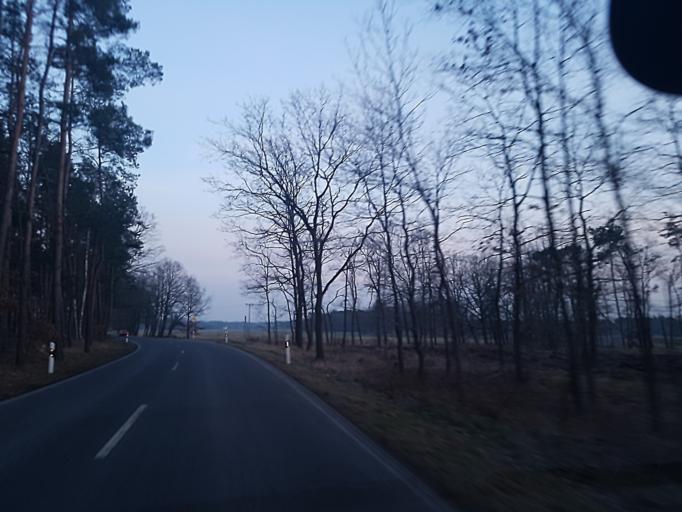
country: DE
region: Saxony-Anhalt
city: Holzdorf
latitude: 51.7569
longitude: 13.1185
